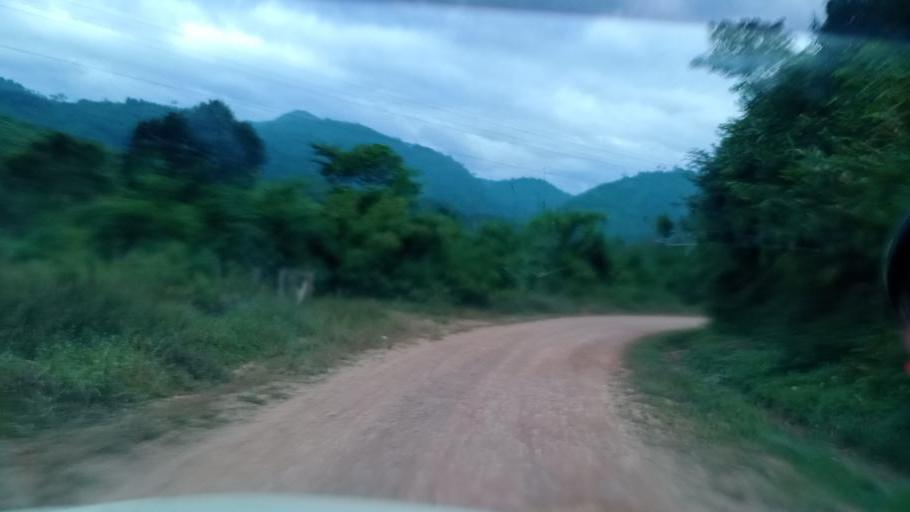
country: TH
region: Changwat Bueng Kan
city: Pak Khat
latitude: 18.7171
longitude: 103.2218
